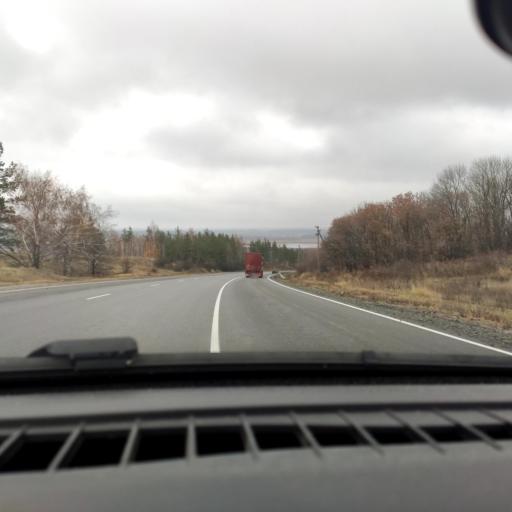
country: RU
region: Voronezj
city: Ostrogozhsk
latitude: 51.0216
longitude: 38.9813
